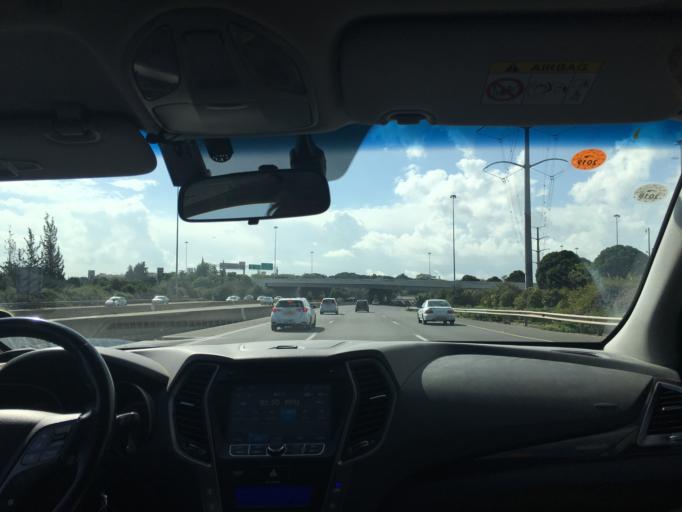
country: IL
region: Tel Aviv
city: Bene Beraq
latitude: 32.0576
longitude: 34.8350
